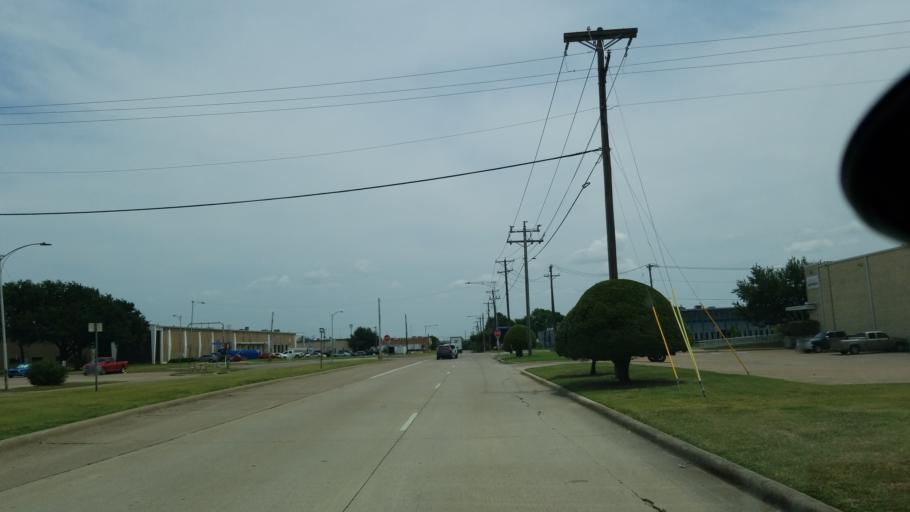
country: US
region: Texas
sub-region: Dallas County
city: Grand Prairie
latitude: 32.7564
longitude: -97.0470
